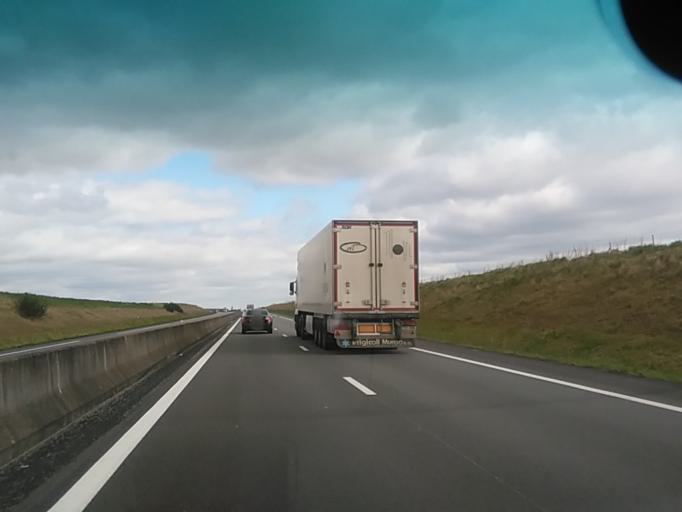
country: FR
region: Haute-Normandie
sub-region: Departement de l'Eure
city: Thiberville
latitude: 49.0962
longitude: 0.4993
